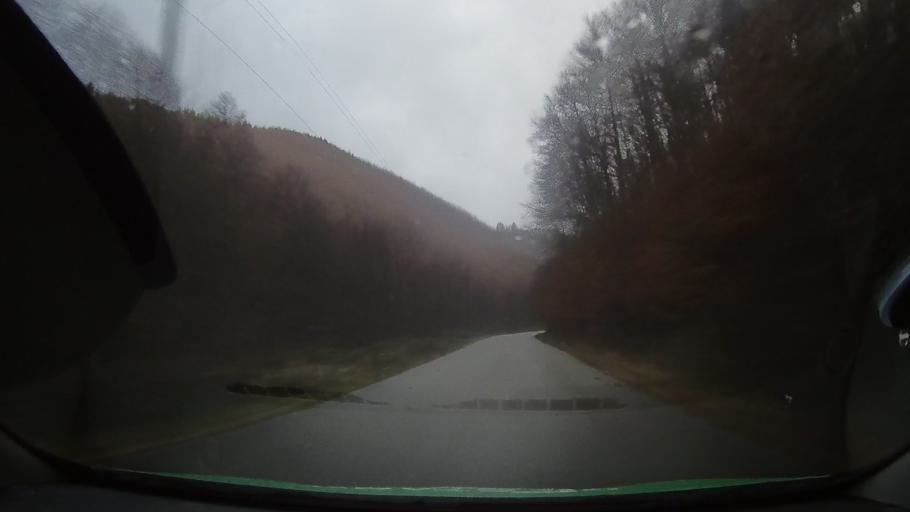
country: RO
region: Hunedoara
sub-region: Comuna Ribita
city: Ribita
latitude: 46.2786
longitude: 22.7392
